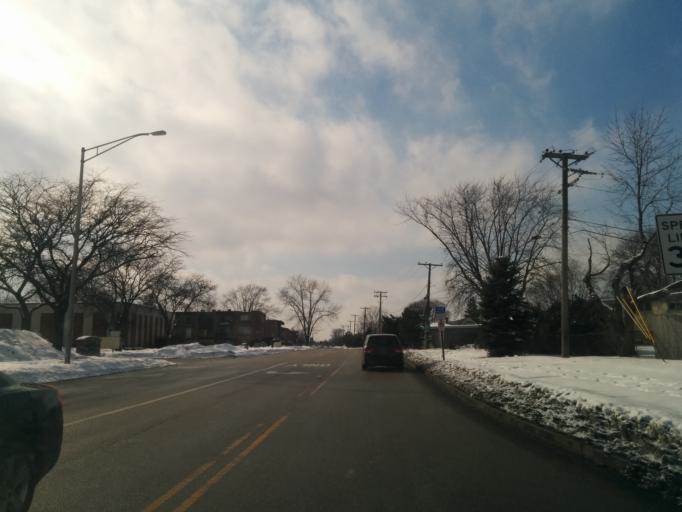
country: US
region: Illinois
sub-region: Cook County
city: Tinley Park
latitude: 41.5733
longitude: -87.7935
